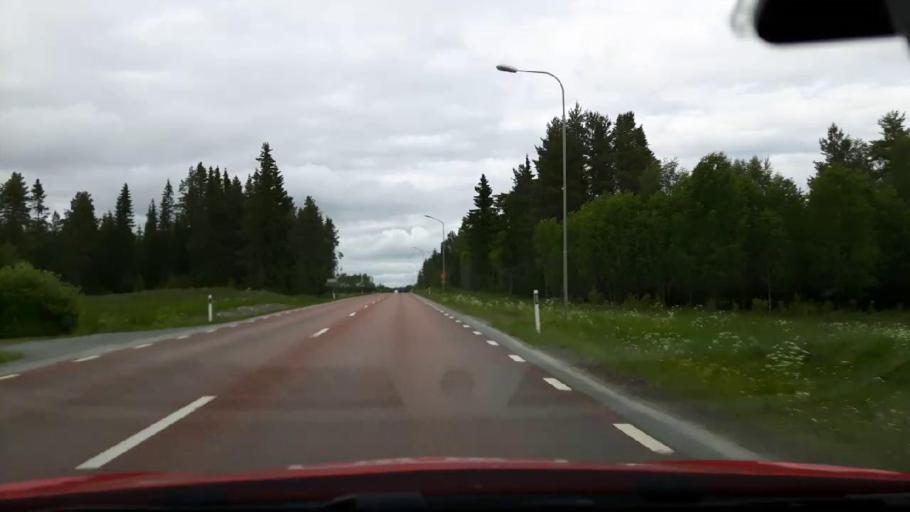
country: SE
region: Jaemtland
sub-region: Bergs Kommun
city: Hoverberg
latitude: 62.9298
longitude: 14.5375
